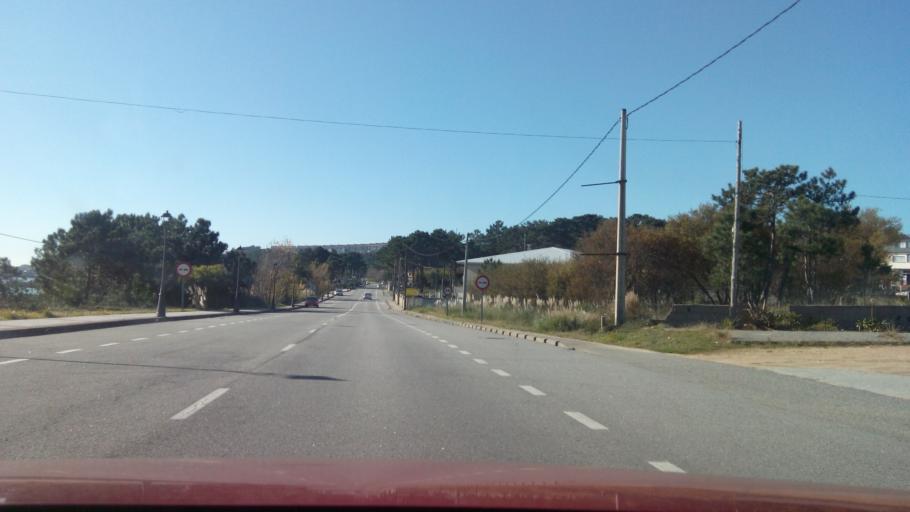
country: ES
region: Galicia
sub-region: Provincia de Pontevedra
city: O Grove
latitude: 42.4640
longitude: -8.9106
